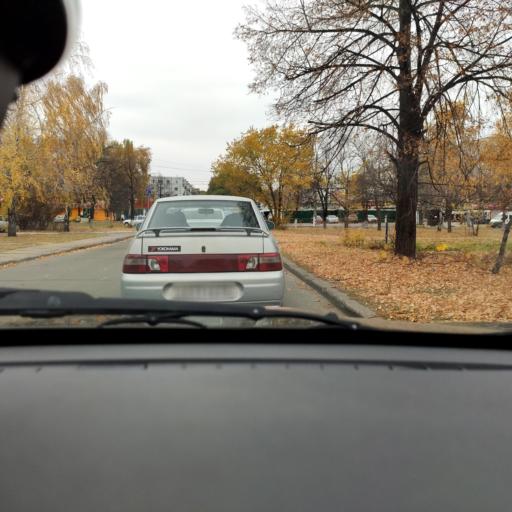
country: RU
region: Samara
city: Tol'yatti
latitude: 53.5261
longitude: 49.2765
